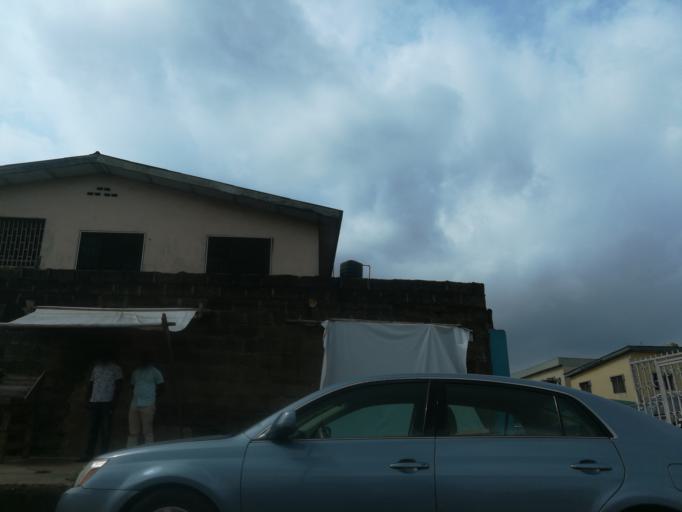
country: NG
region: Lagos
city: Ikeja
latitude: 6.6234
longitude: 3.3556
